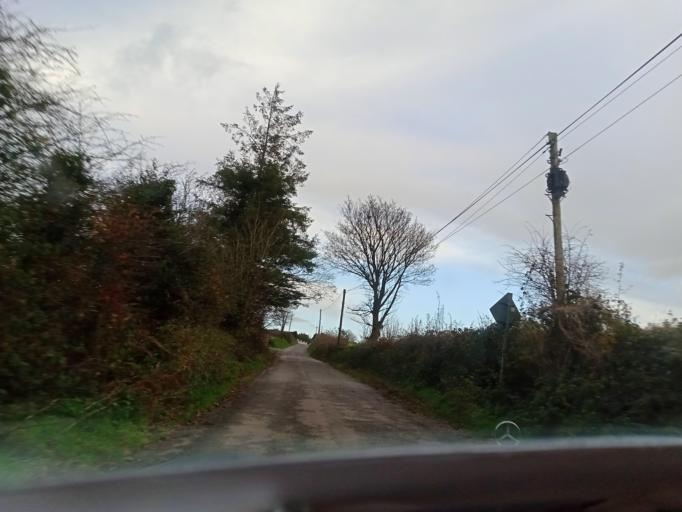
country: IE
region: Munster
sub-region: Waterford
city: Waterford
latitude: 52.3331
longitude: -7.0364
